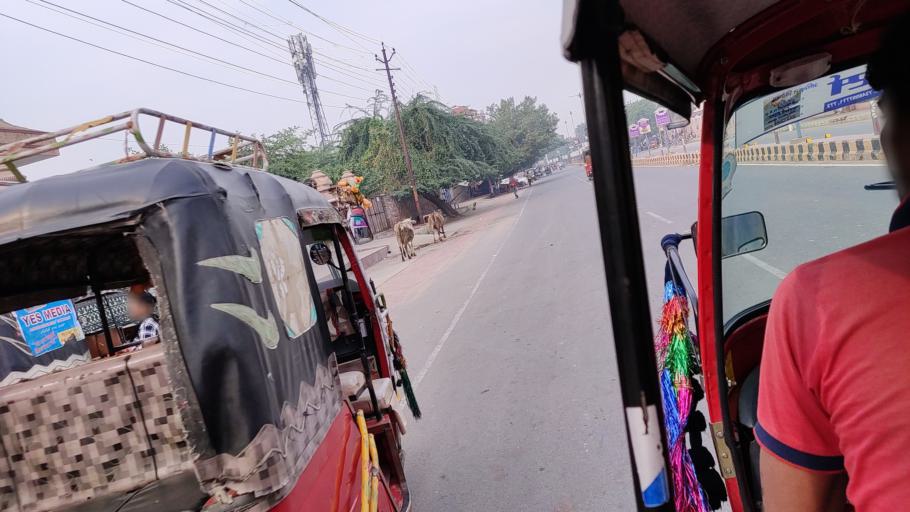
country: IN
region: Uttar Pradesh
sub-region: Mathura
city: Vrindavan
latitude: 27.5707
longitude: 77.6691
